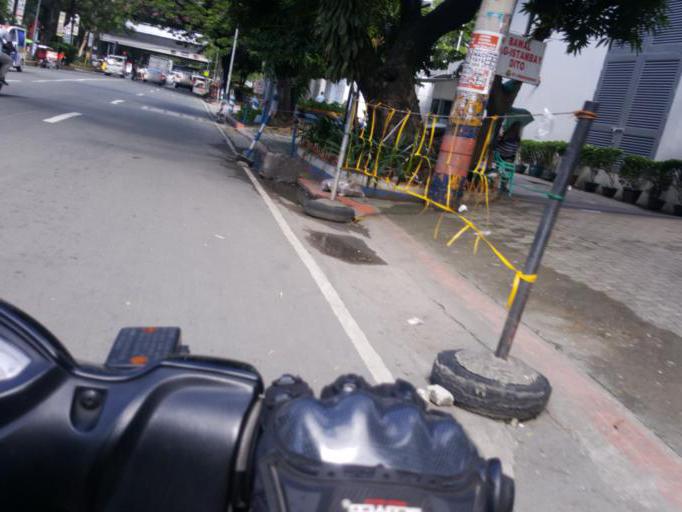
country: PH
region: Metro Manila
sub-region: City of Manila
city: Port Area
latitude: 14.5818
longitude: 120.9835
